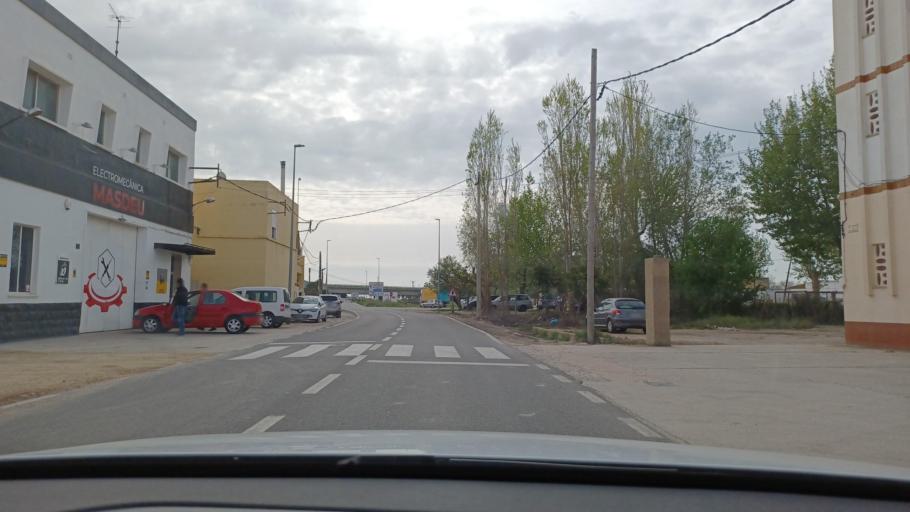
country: ES
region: Catalonia
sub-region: Provincia de Tarragona
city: Amposta
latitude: 40.7097
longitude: 0.5869
